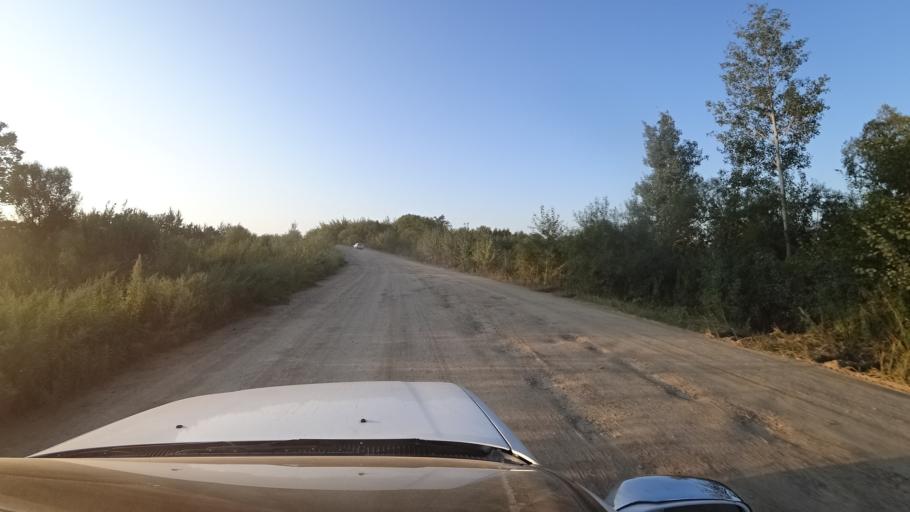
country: RU
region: Primorskiy
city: Dal'nerechensk
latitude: 45.9414
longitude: 133.7612
